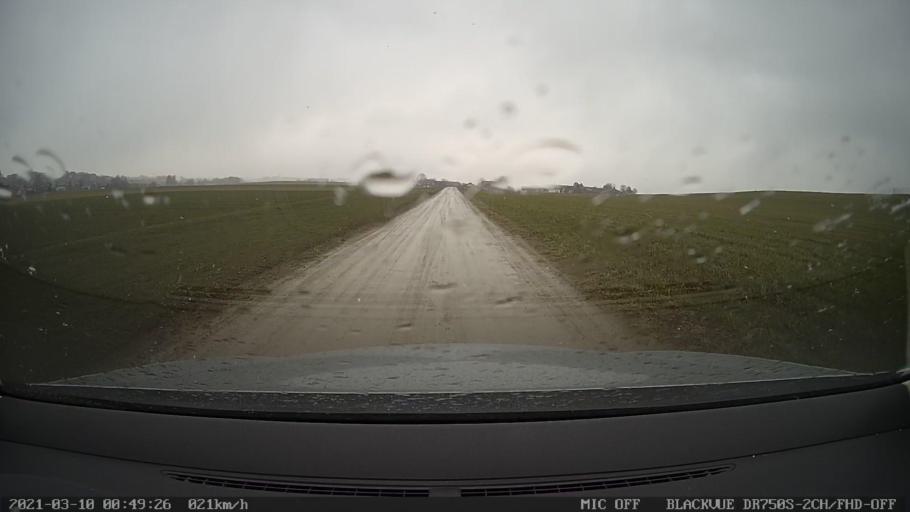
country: DE
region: Bavaria
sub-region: Upper Bavaria
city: Griesstatt
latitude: 47.9914
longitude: 12.1874
